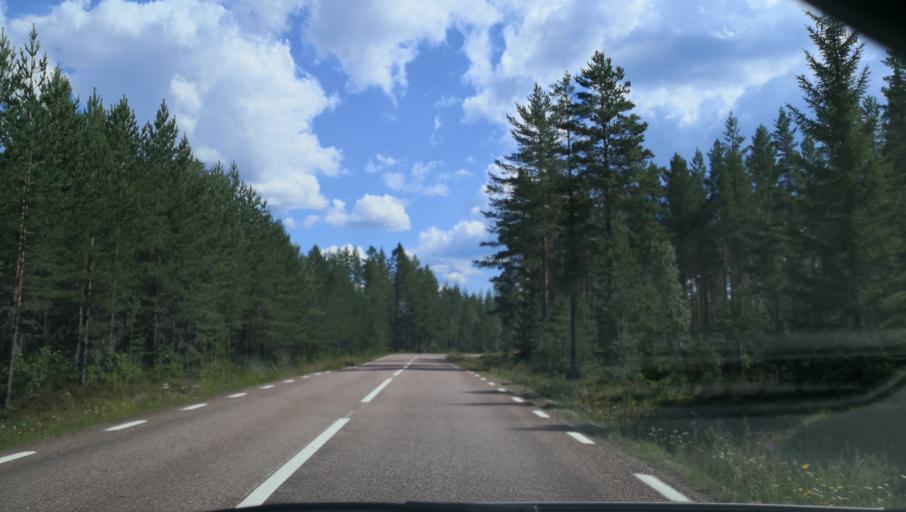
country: SE
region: Dalarna
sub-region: Rattviks Kommun
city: Vikarbyn
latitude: 61.1518
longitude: 15.0968
